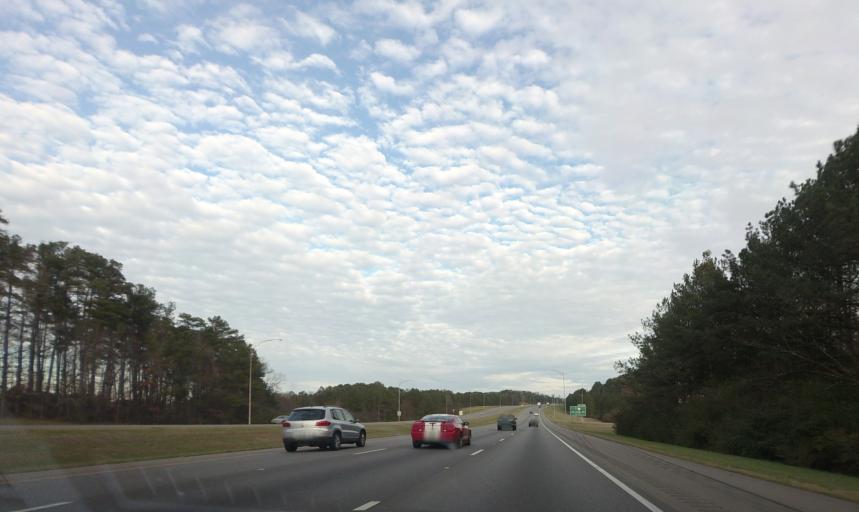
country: US
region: Alabama
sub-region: Jefferson County
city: Irondale
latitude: 33.5448
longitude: -86.6729
